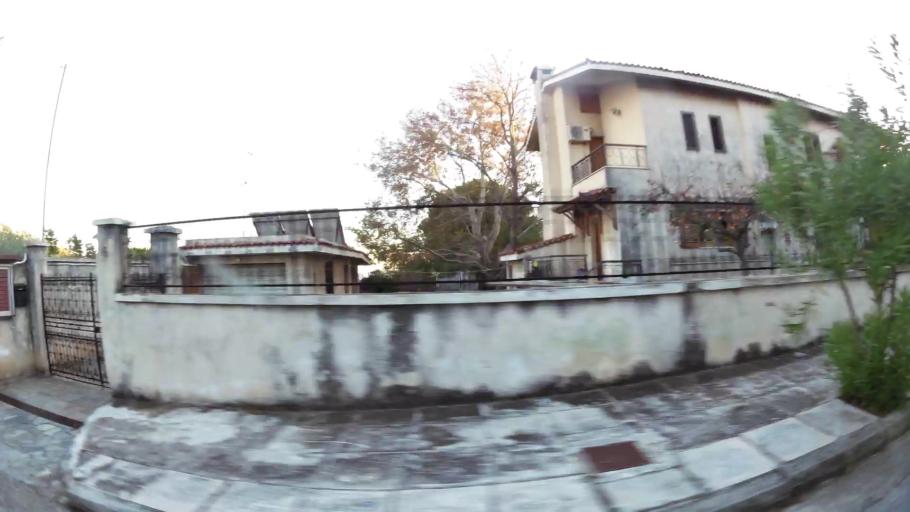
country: GR
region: Attica
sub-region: Nomarchia Athinas
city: Nea Penteli
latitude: 38.0523
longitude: 23.8540
